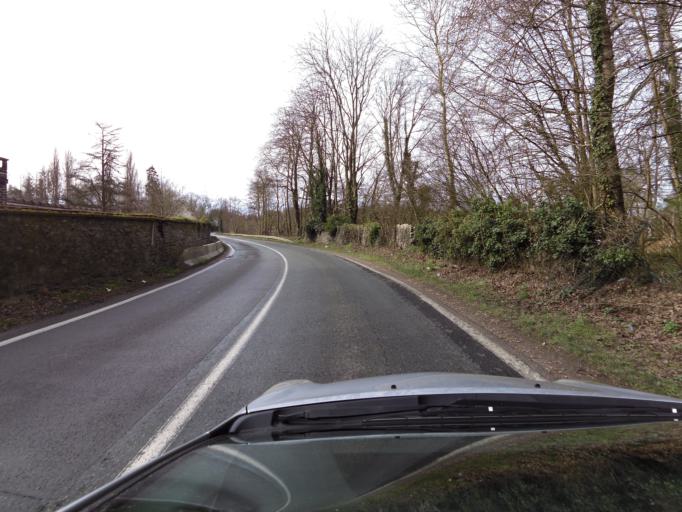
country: FR
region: Picardie
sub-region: Departement de l'Oise
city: Ver-sur-Launette
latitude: 49.1328
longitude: 2.6916
